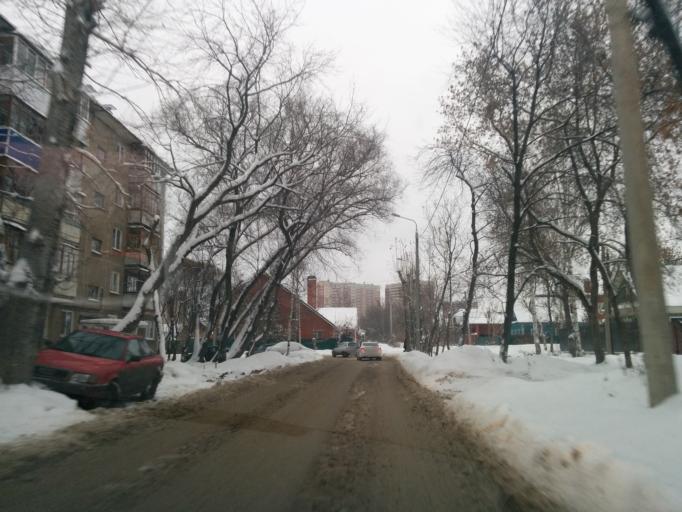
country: RU
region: Perm
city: Perm
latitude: 57.9808
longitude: 56.2957
